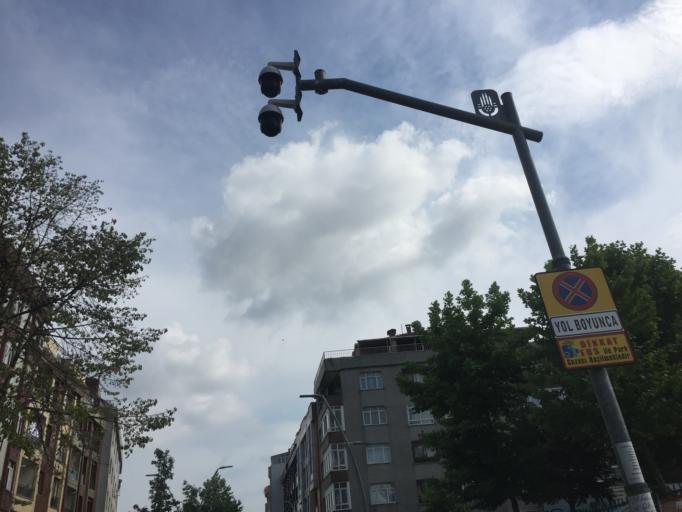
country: TR
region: Istanbul
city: Zeytinburnu
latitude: 41.0008
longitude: 28.9042
